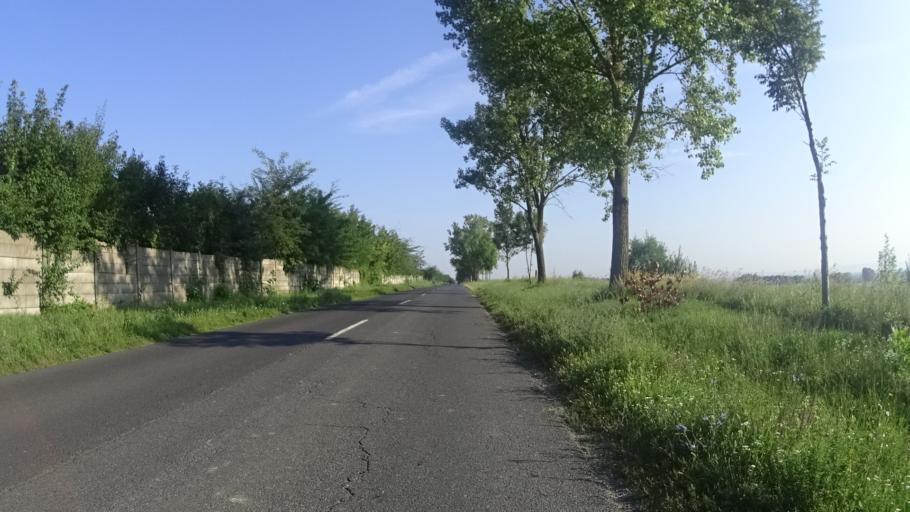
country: HU
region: Zala
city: Sarmellek
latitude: 46.6845
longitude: 17.1693
